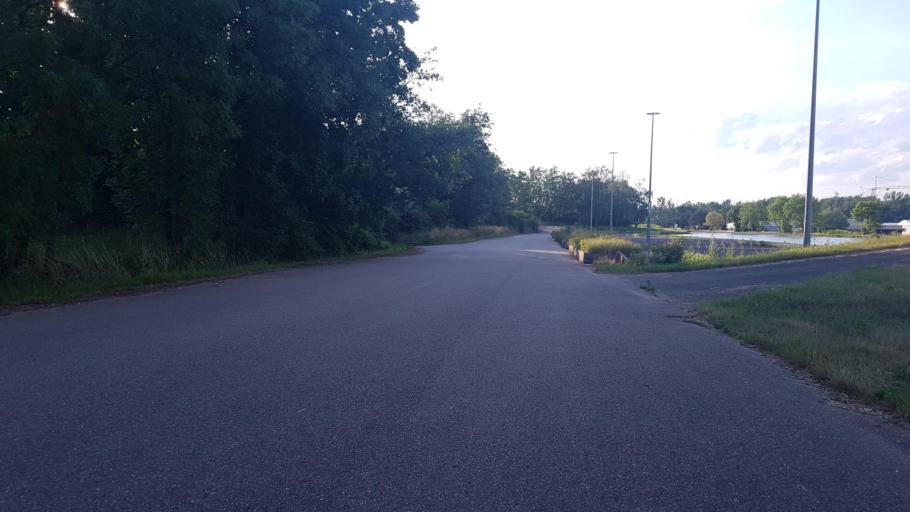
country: FR
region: Alsace
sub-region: Departement du Bas-Rhin
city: Dettwiller
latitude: 48.7504
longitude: 7.4518
